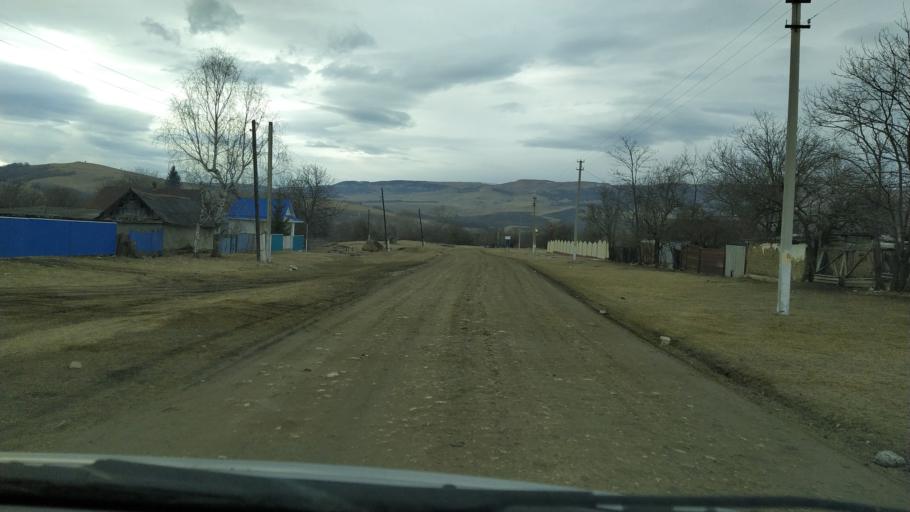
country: RU
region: Krasnodarskiy
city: Peredovaya
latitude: 44.0840
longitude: 41.3662
